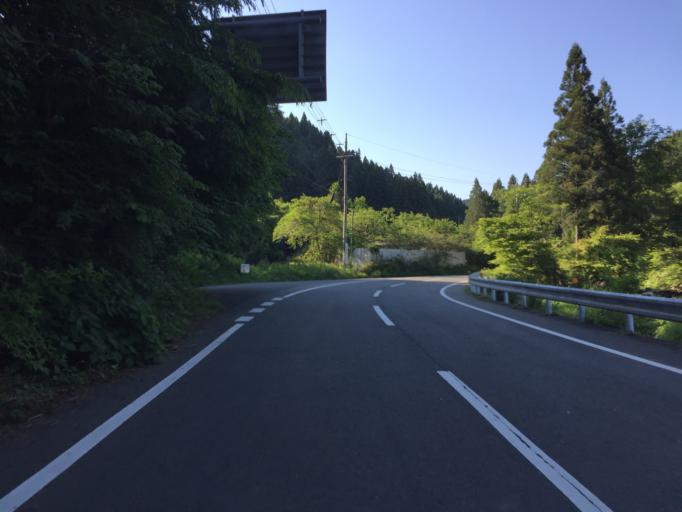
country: JP
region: Ibaraki
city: Kitaibaraki
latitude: 36.8641
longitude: 140.6373
